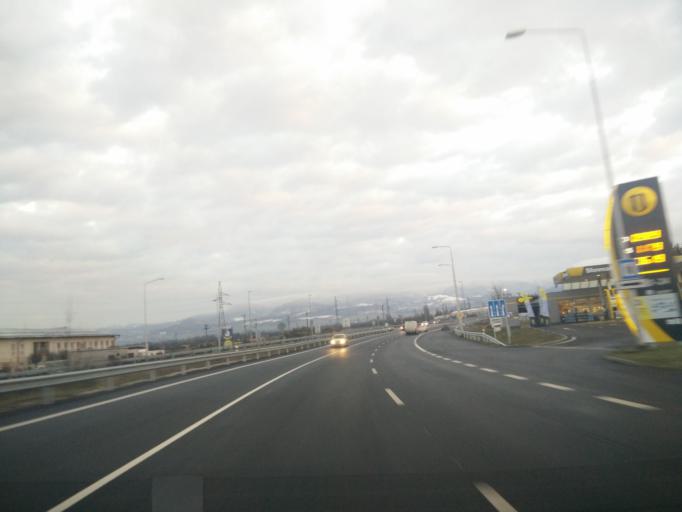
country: SK
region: Nitriansky
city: Novaky
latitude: 48.7245
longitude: 18.5531
